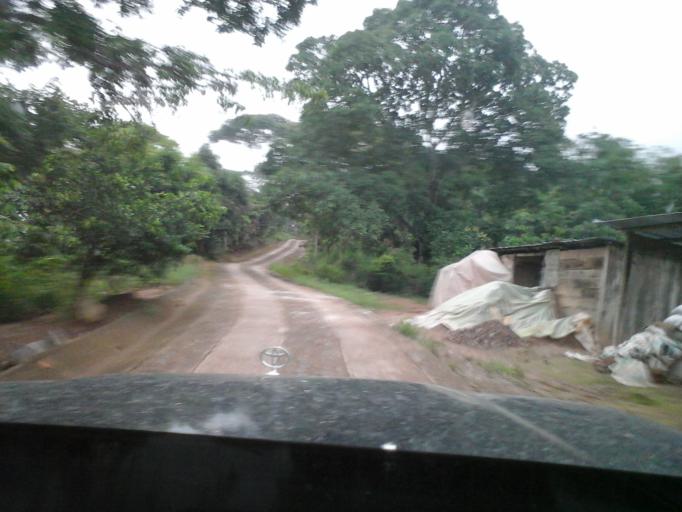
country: CO
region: Cesar
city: Agustin Codazzi
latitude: 9.9401
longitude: -73.1305
